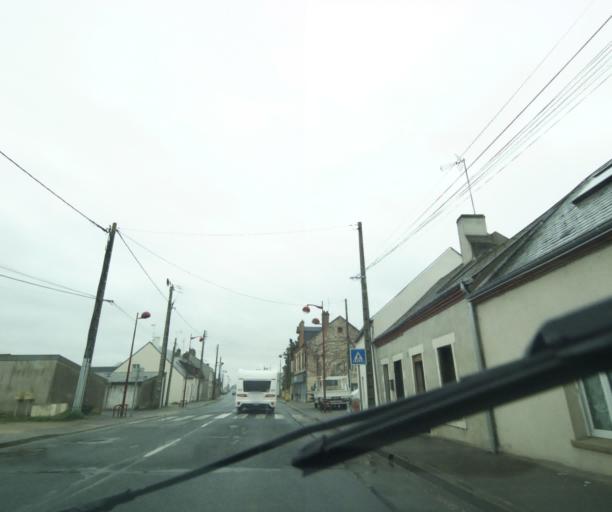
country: FR
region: Centre
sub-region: Departement du Loiret
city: Saran
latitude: 47.9844
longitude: 1.8829
